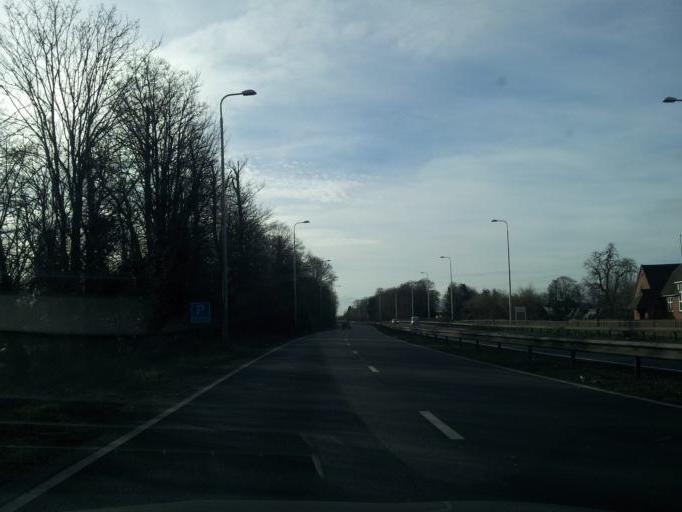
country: GB
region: England
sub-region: Central Bedfordshire
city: Tempsford
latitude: 52.1679
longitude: -0.3012
